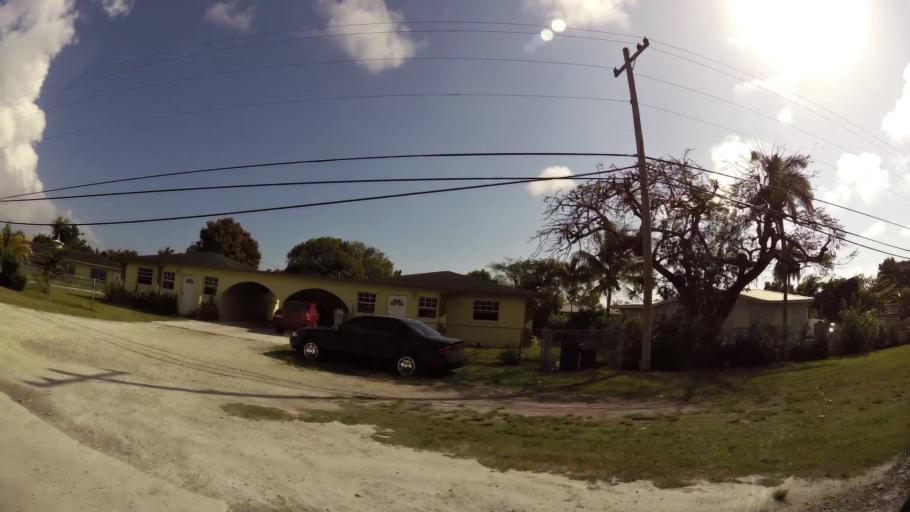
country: BS
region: Freeport
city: Freeport
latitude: 26.5225
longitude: -78.6894
